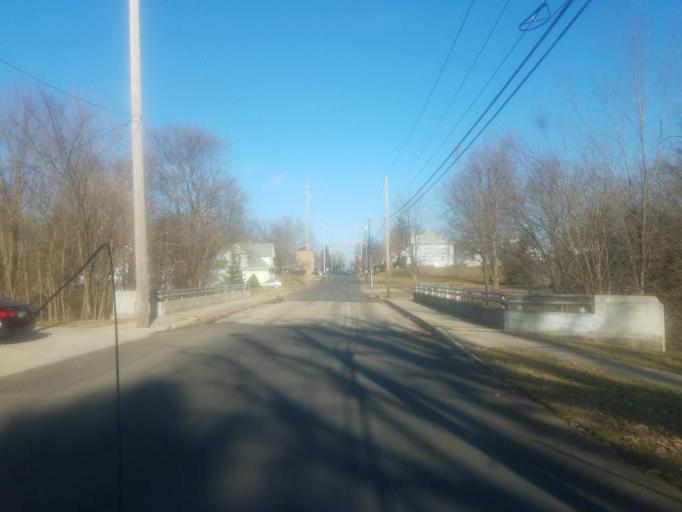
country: US
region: Ohio
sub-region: Crawford County
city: Galion
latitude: 40.7373
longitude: -82.7834
